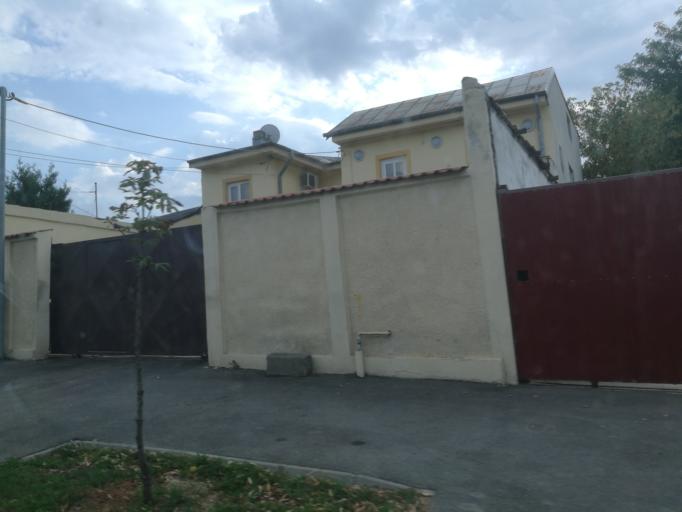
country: RO
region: Ilfov
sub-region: Comuna Mogosoaia
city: Mogosoaia
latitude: 44.5018
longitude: 26.0260
